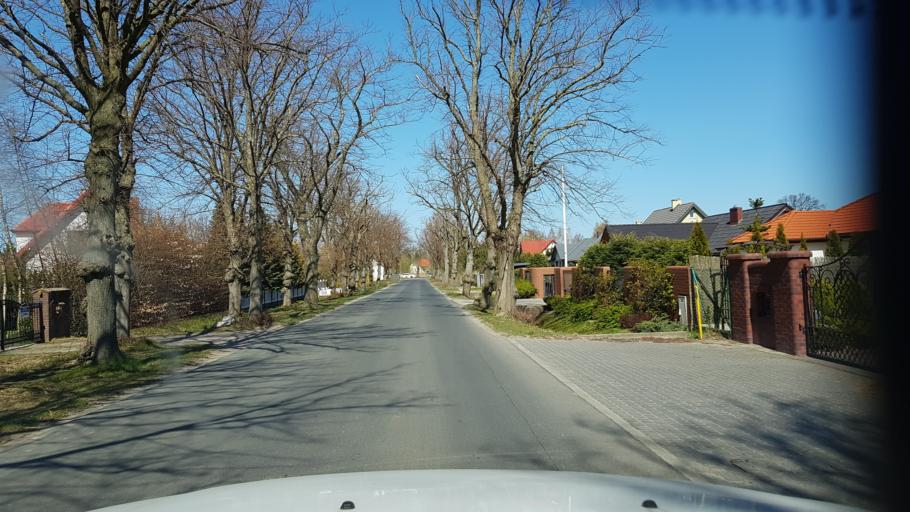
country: PL
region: West Pomeranian Voivodeship
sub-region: Koszalin
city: Koszalin
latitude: 54.2393
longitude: 16.1630
